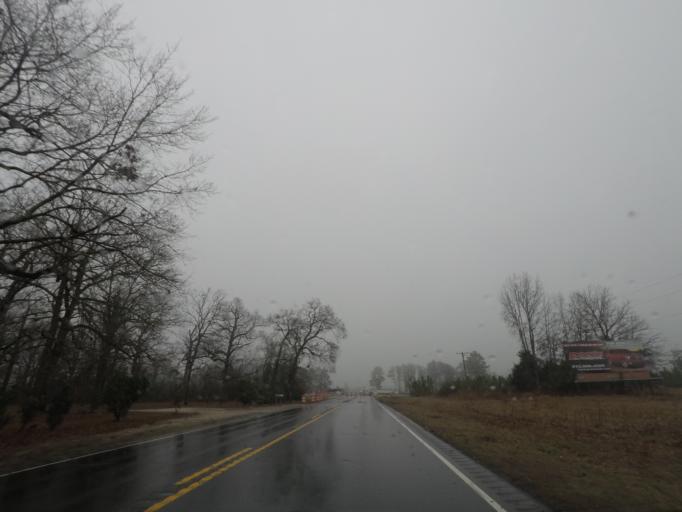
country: US
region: North Carolina
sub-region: Scotland County
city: Laurinburg
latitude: 34.8431
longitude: -79.4589
